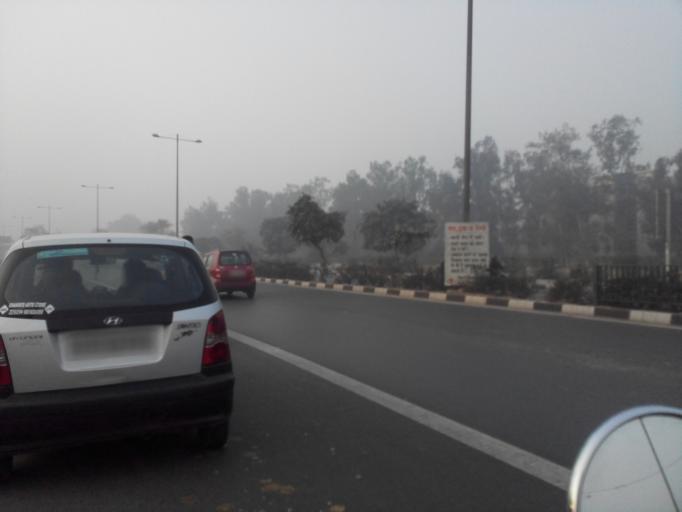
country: IN
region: Uttar Pradesh
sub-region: Gautam Buddha Nagar
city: Noida
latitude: 28.6629
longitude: 77.3209
